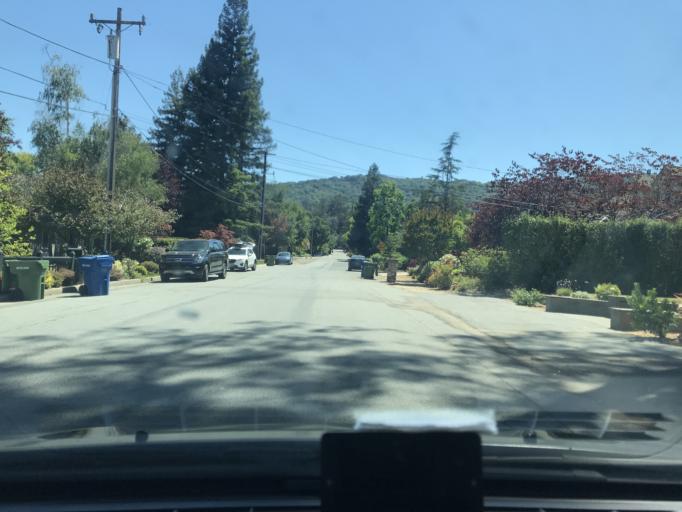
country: US
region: California
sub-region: Santa Clara County
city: Monte Sereno
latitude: 37.2351
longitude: -121.9842
